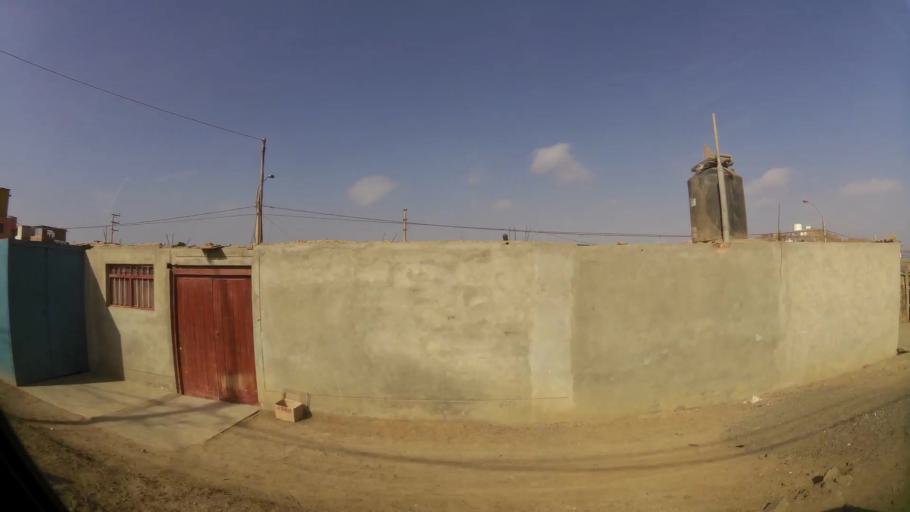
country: PE
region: Lima
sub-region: Huaura
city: Huacho
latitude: -11.1273
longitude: -77.6173
